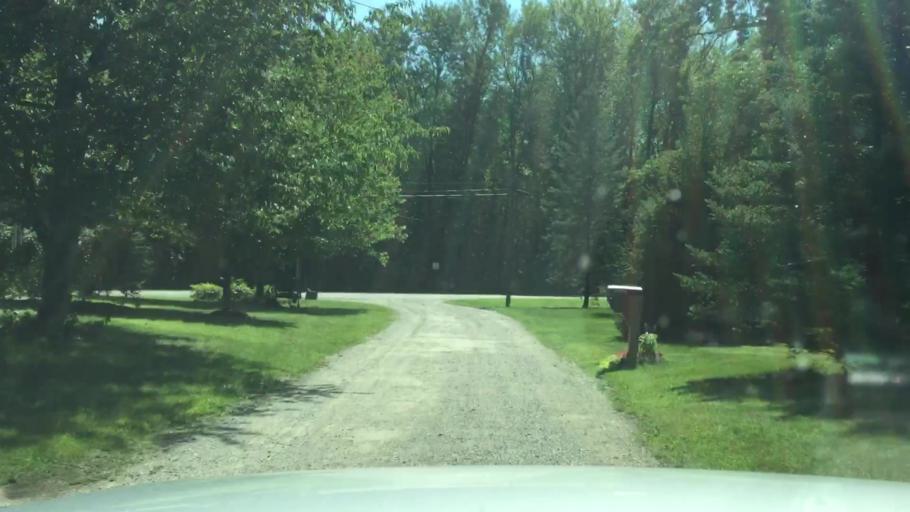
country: US
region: Michigan
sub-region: Lenawee County
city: Manitou Beach-Devils Lake
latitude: 41.9849
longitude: -84.2812
